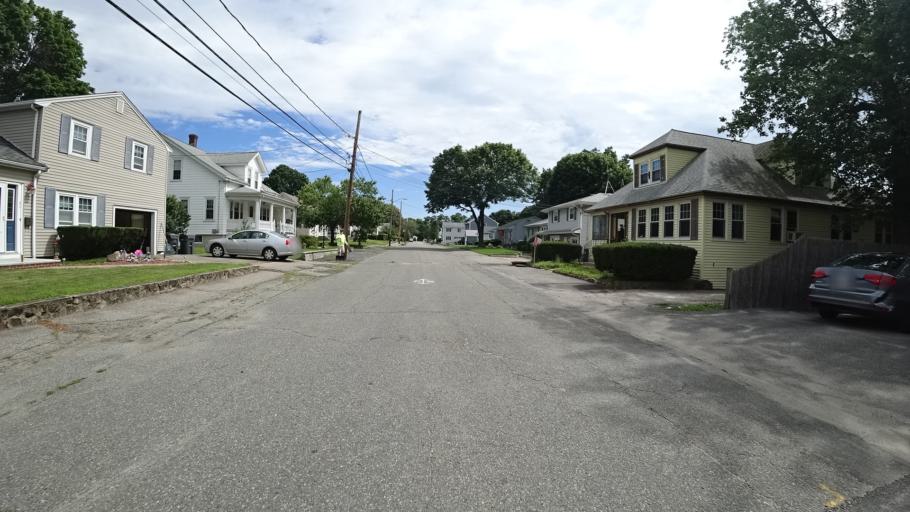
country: US
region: Massachusetts
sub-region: Norfolk County
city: Dedham
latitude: 42.2281
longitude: -71.1437
